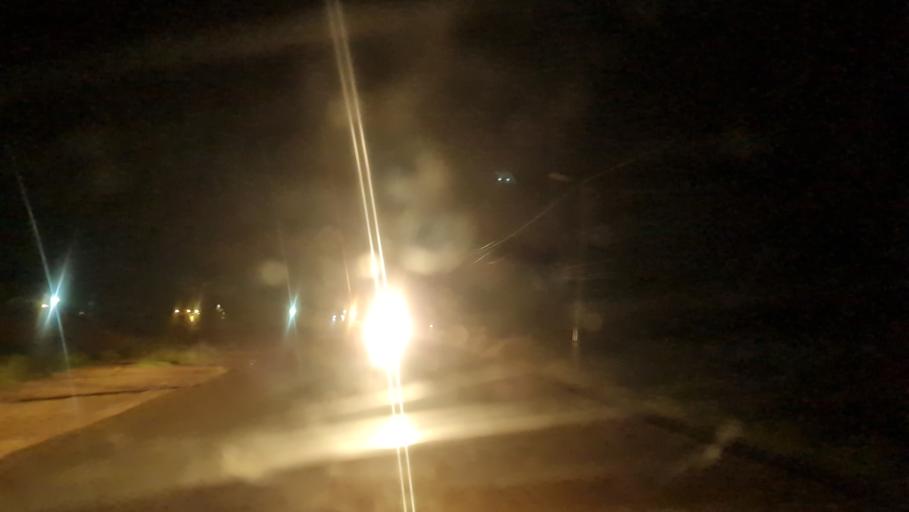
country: MZ
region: Nampula
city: Nacala
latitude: -14.6503
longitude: 40.6834
